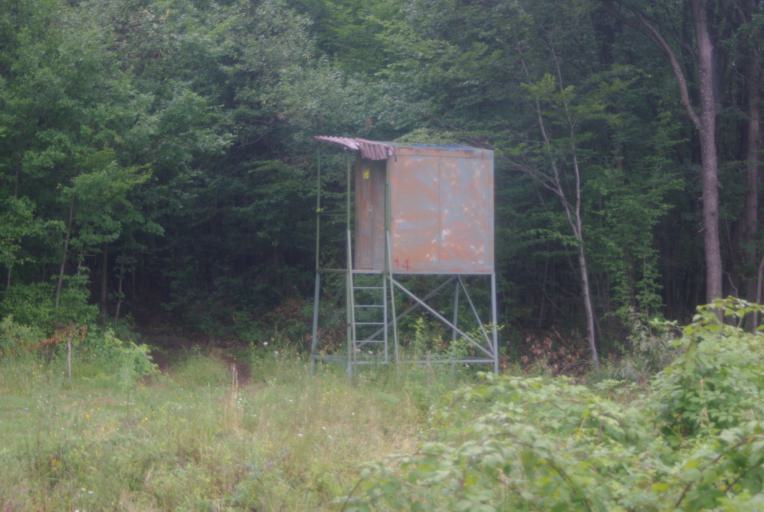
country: HU
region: Borsod-Abauj-Zemplen
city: Gonc
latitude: 48.3944
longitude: 21.3574
